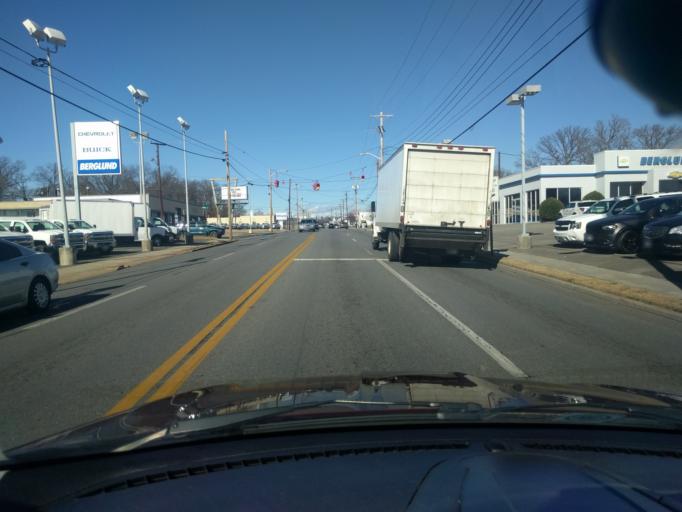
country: US
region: Virginia
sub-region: City of Roanoke
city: Roanoke
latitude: 37.2897
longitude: -79.9343
